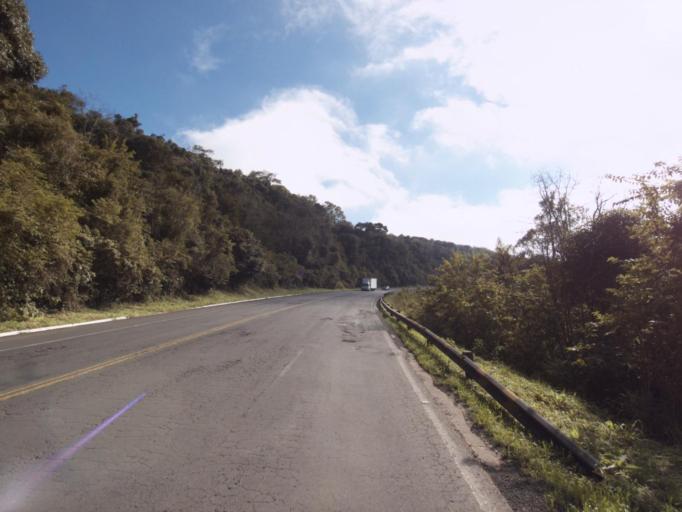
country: BR
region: Rio Grande do Sul
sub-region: Frederico Westphalen
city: Frederico Westphalen
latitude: -27.1333
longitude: -53.2130
